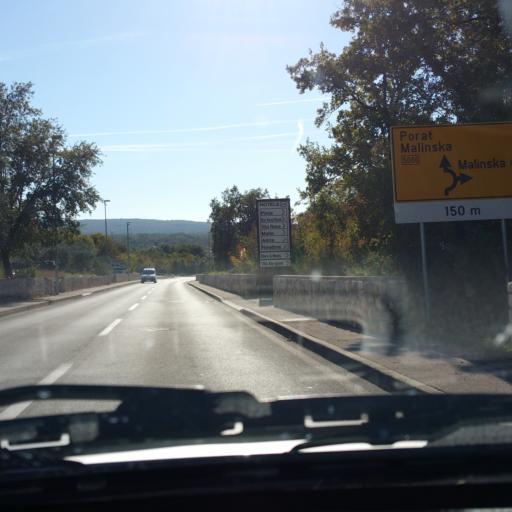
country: HR
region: Primorsko-Goranska
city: Njivice
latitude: 45.1279
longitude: 14.5388
